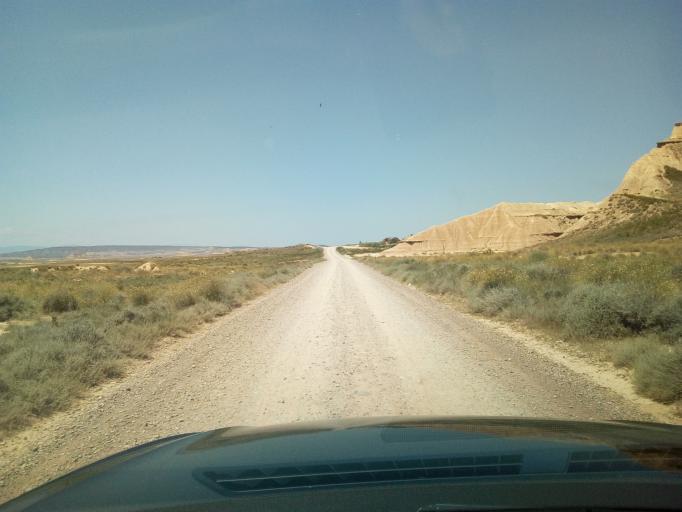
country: ES
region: Aragon
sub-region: Provincia de Zaragoza
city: Sadaba
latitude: 42.1951
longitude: -1.4180
